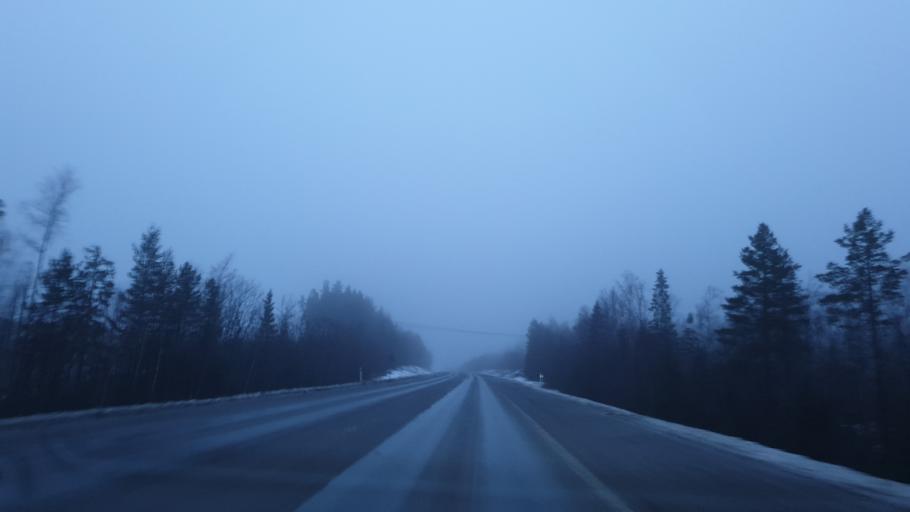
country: SE
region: Vaesterbotten
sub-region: Umea Kommun
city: Holmsund
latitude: 63.7694
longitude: 20.3361
